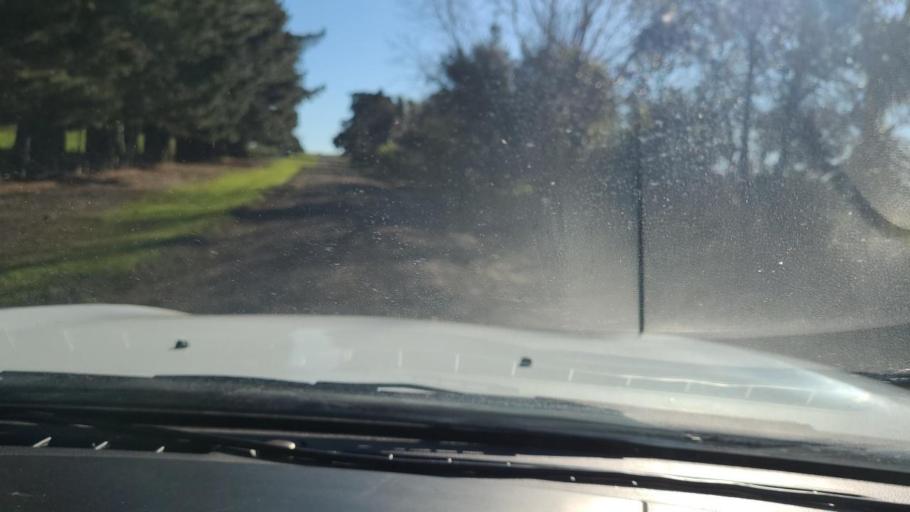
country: NZ
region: Hawke's Bay
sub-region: Napier City
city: Taradale
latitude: -39.4584
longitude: 176.6314
